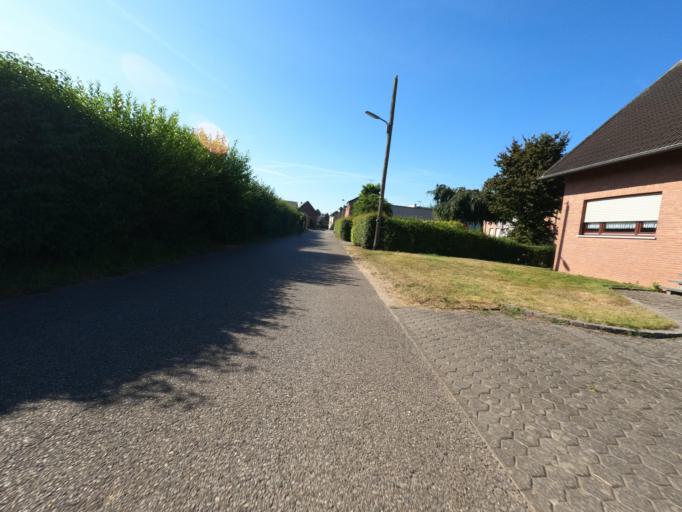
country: DE
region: North Rhine-Westphalia
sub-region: Regierungsbezirk Koln
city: Heinsberg
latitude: 51.0754
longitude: 6.1269
